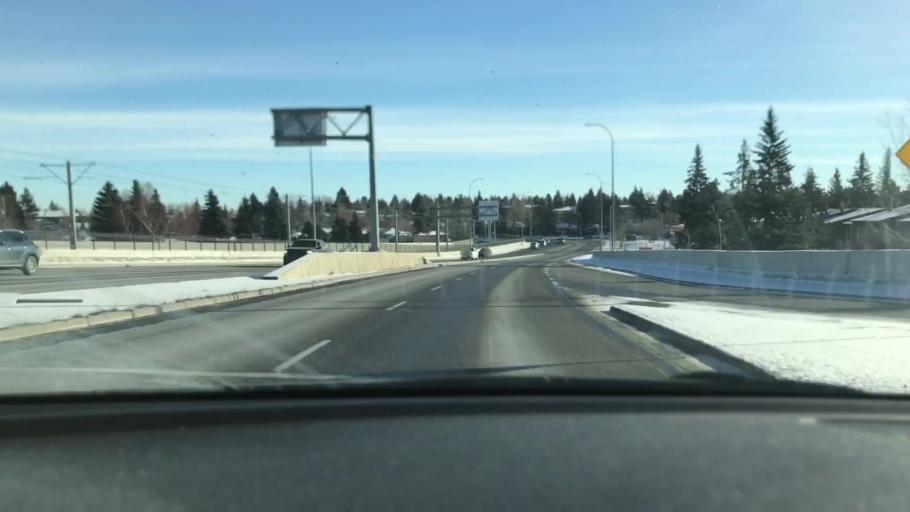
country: CA
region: Alberta
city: Calgary
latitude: 51.0394
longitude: -114.1619
